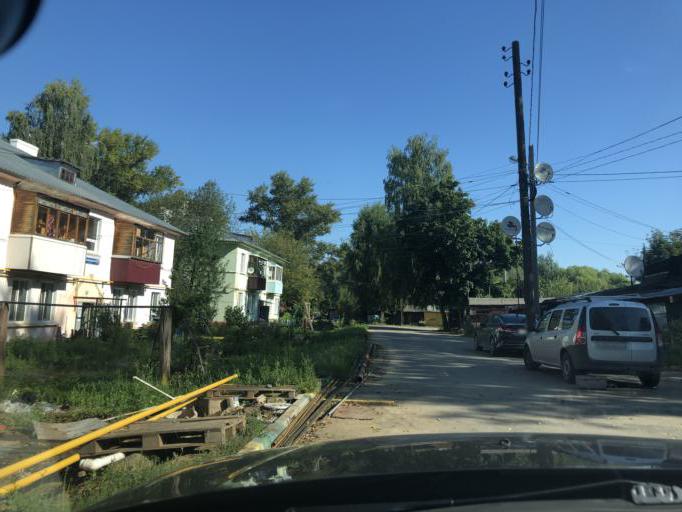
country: RU
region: Tula
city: Mendeleyevskiy
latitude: 54.1688
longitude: 37.5599
